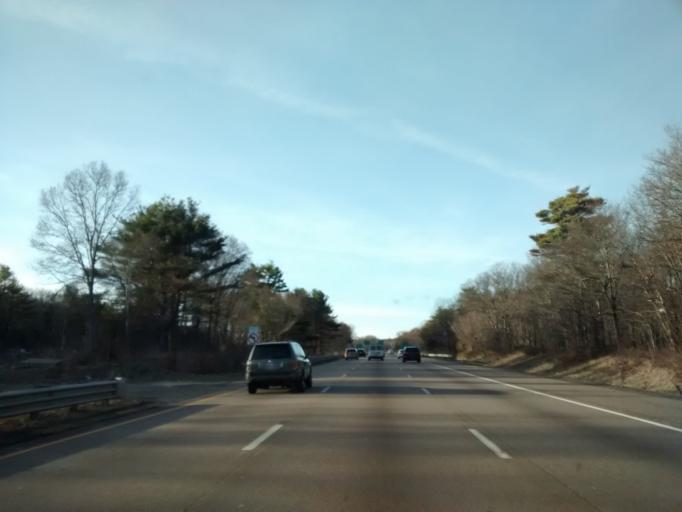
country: US
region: Massachusetts
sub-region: Norfolk County
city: Randolph
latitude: 42.1940
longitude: -71.0776
